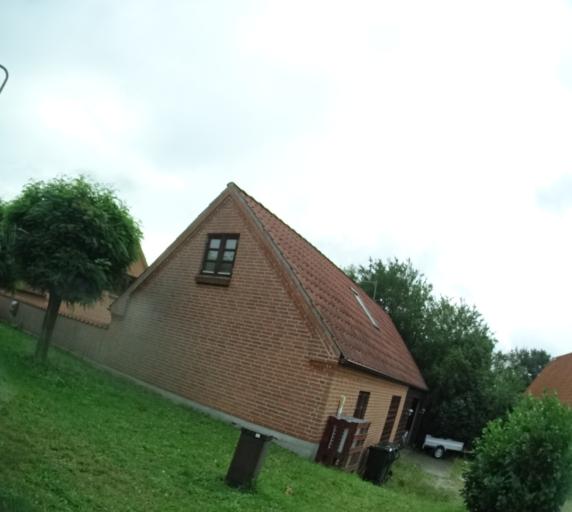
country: DK
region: Central Jutland
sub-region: Syddjurs Kommune
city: Ronde
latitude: 56.3448
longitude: 10.4572
